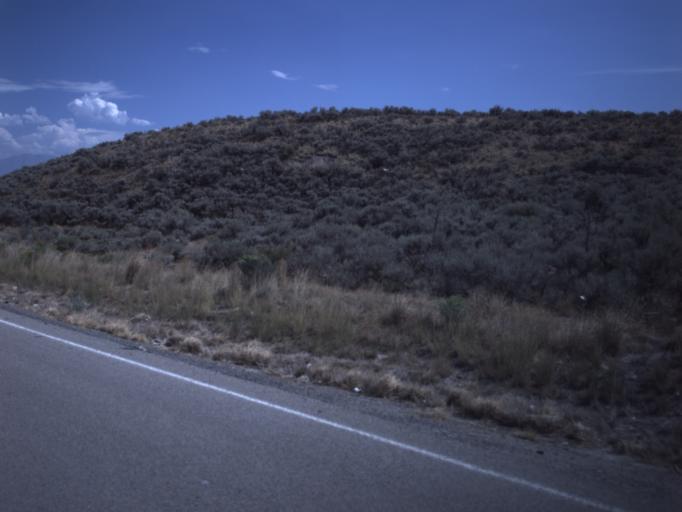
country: US
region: Utah
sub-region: Utah County
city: Eagle Mountain
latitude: 40.3801
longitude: -111.9911
